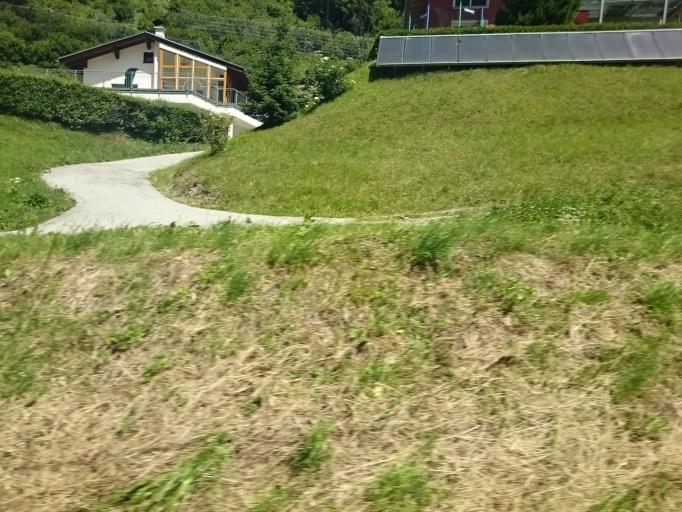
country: AT
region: Tyrol
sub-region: Politischer Bezirk Innsbruck Land
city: Gries am Brenner
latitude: 47.0634
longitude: 11.4973
